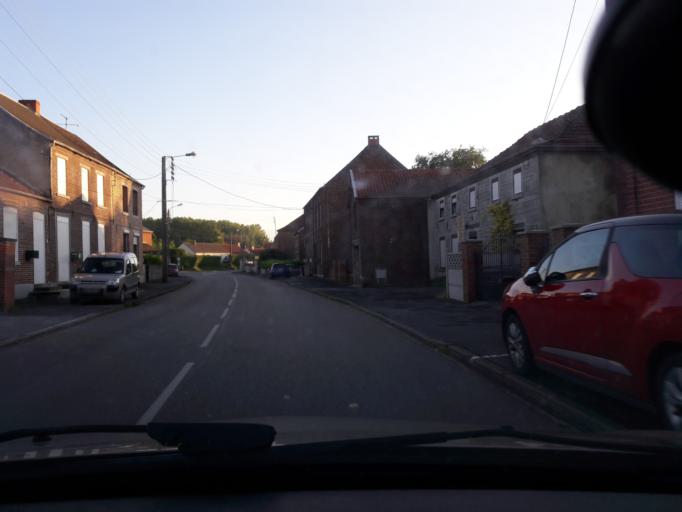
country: FR
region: Nord-Pas-de-Calais
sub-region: Departement du Nord
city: Marpent
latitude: 50.2904
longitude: 4.0779
